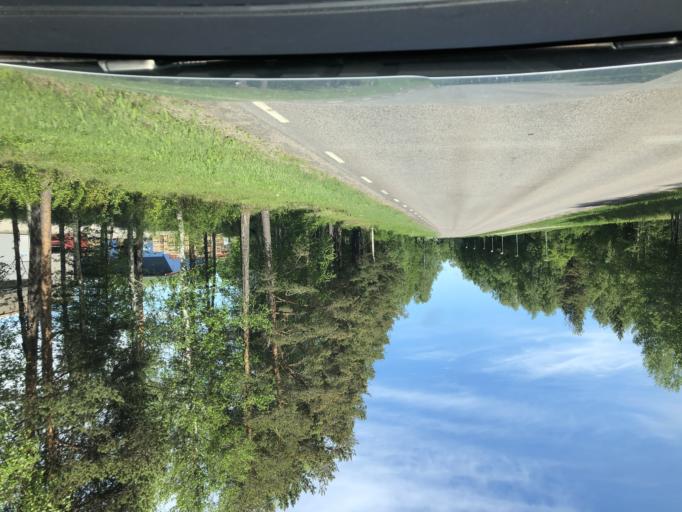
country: SE
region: Norrbotten
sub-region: Pitea Kommun
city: Bergsviken
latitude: 65.3345
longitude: 21.4158
